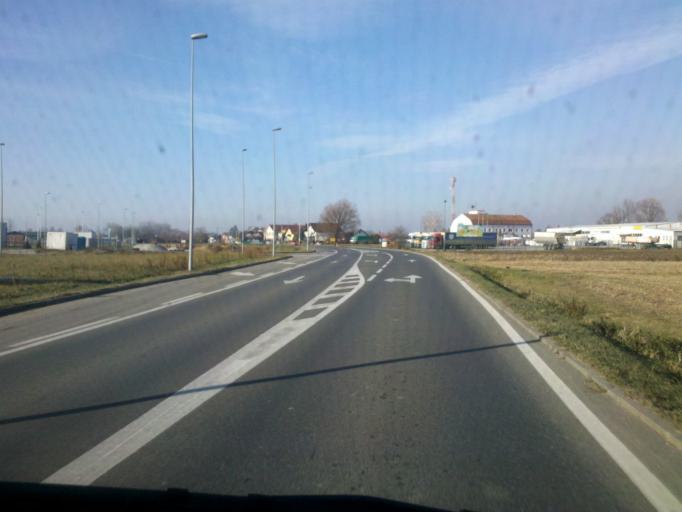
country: HR
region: Koprivnicko-Krizevacka
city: Kalinovac
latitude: 46.0264
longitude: 17.0761
